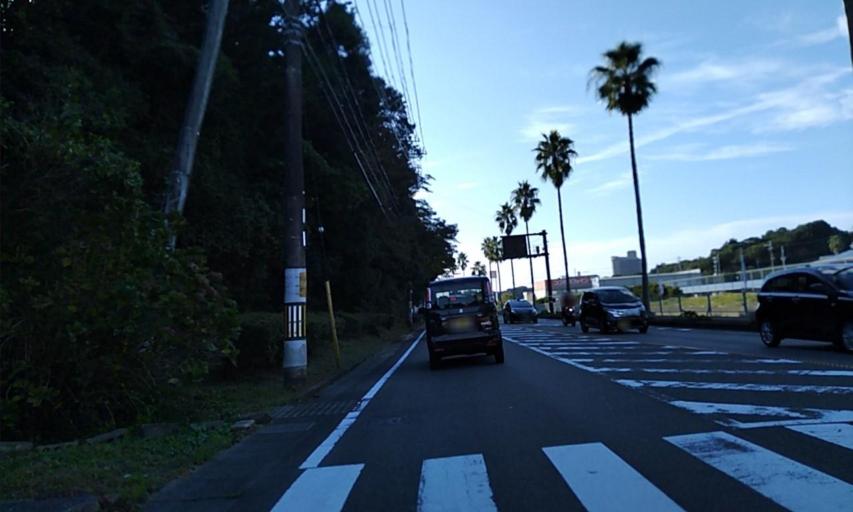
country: JP
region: Wakayama
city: Tanabe
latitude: 33.6796
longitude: 135.3679
